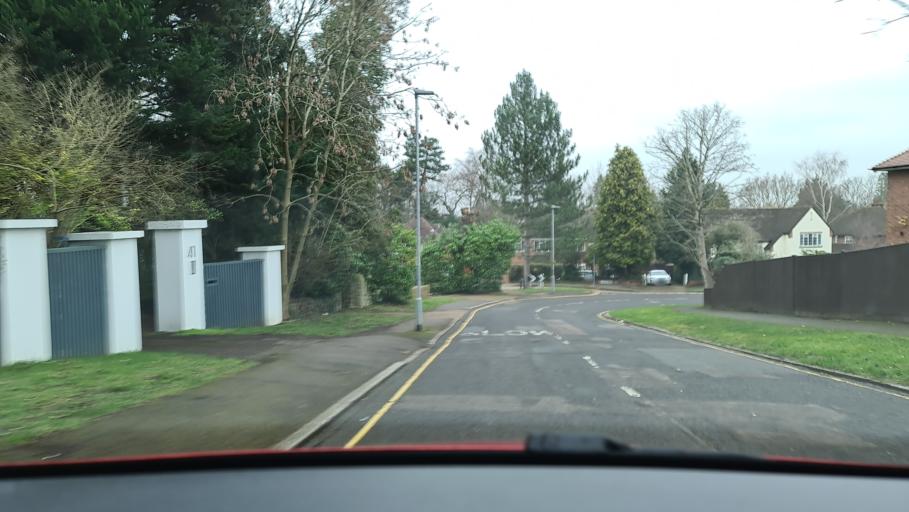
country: GB
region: England
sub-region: Surrey
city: Ditton Hill
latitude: 51.3853
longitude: -0.3099
